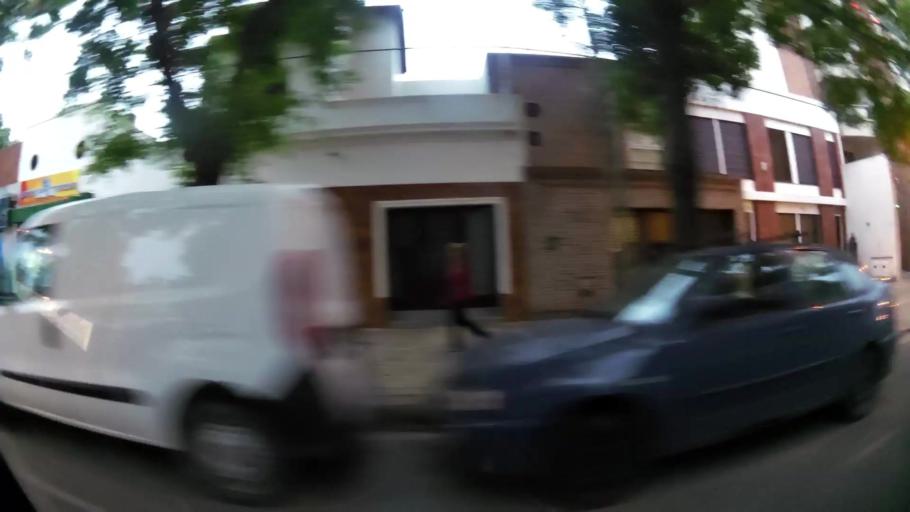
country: AR
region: Buenos Aires
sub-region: Partido de La Plata
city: La Plata
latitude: -34.9197
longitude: -57.9653
